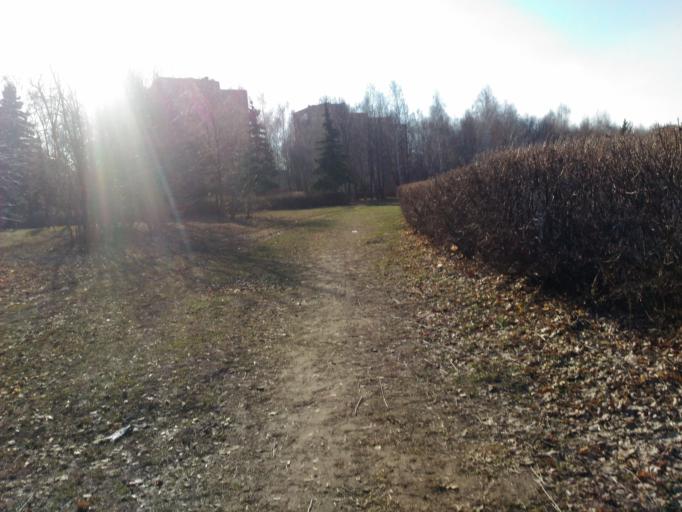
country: RU
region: Ulyanovsk
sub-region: Ulyanovskiy Rayon
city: Ulyanovsk
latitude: 54.3456
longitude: 48.3976
